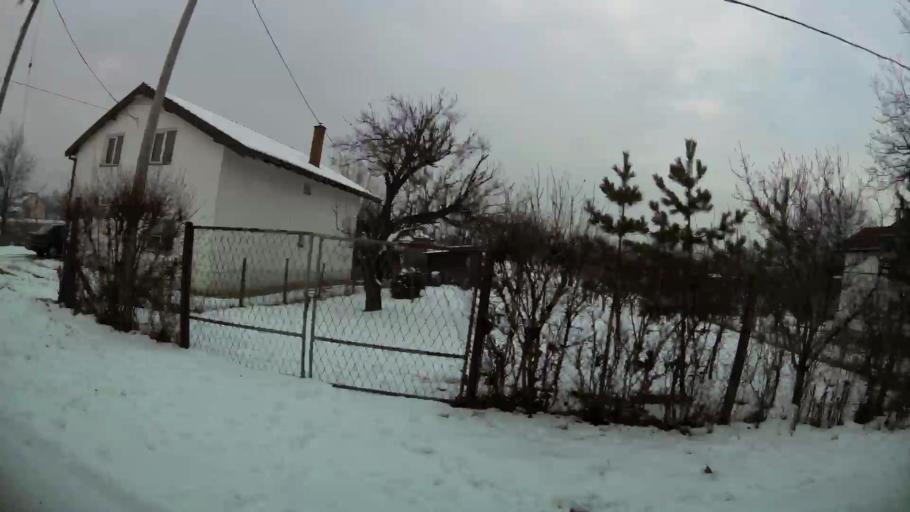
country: MK
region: Saraj
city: Saraj
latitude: 42.0389
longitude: 21.3589
